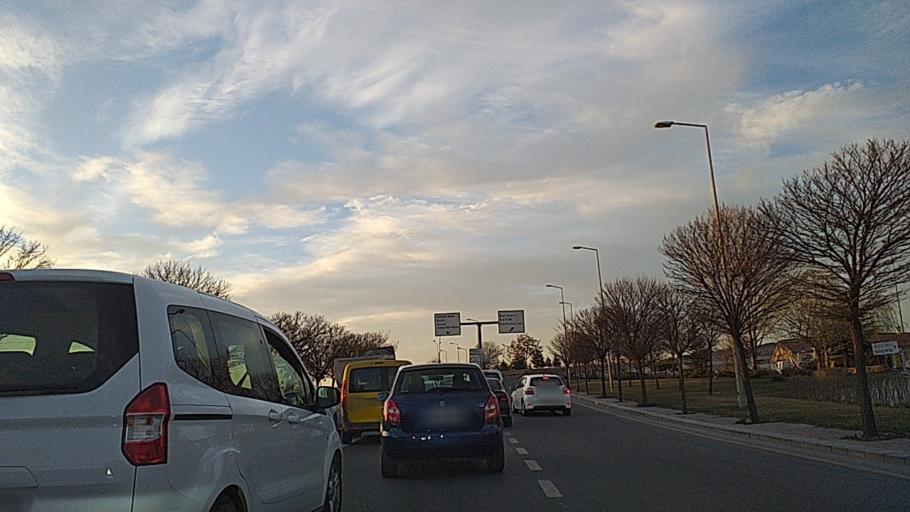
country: TR
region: Ankara
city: Batikent
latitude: 39.9622
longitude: 32.6851
